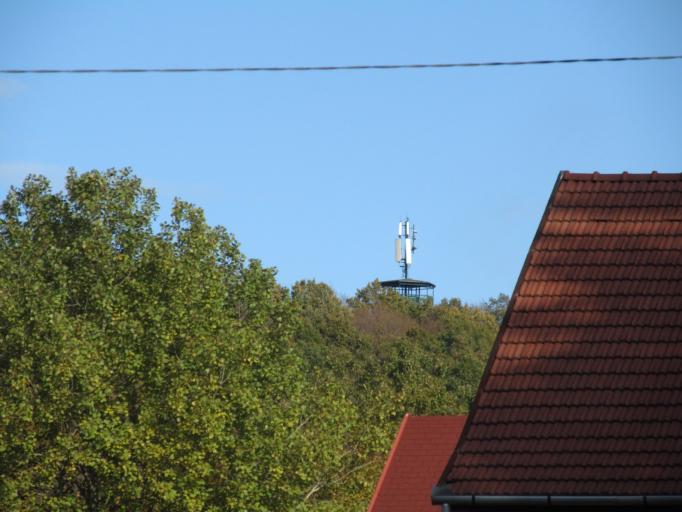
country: HU
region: Nograd
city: Batonyterenye
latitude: 47.9269
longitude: 19.8740
